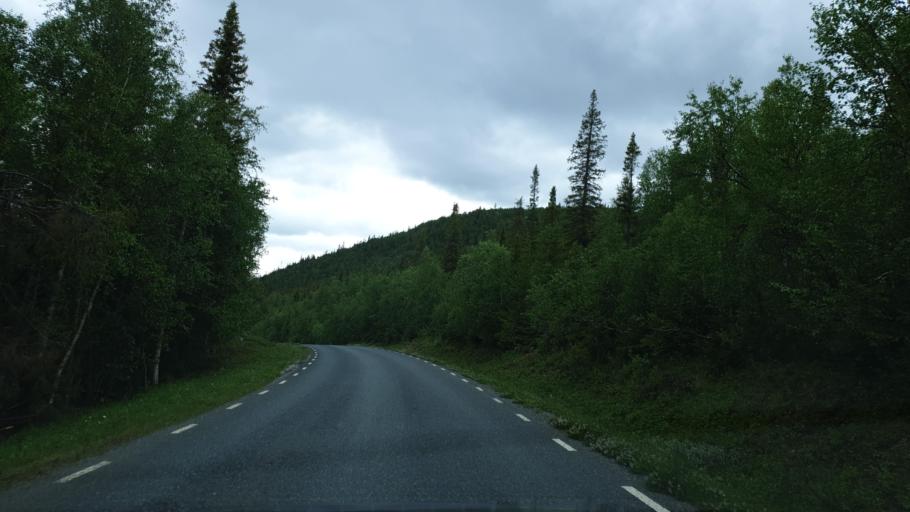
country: SE
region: Vaesterbotten
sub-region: Vilhelmina Kommun
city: Sjoberg
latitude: 65.2572
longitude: 15.4028
